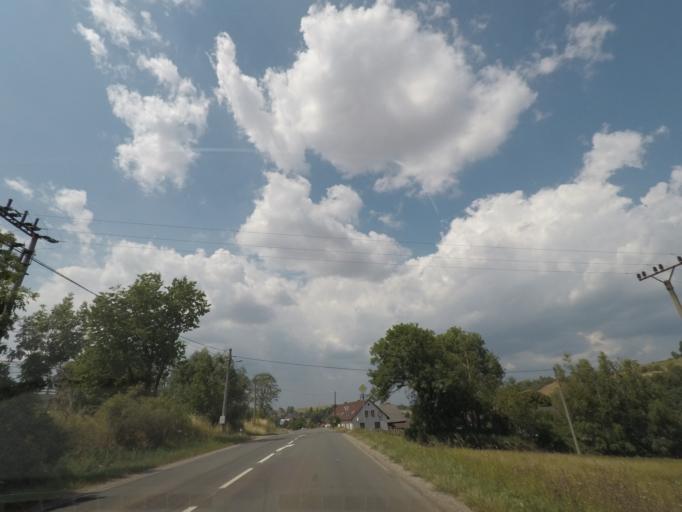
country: CZ
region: Kralovehradecky
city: Zadni Mostek
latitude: 50.5399
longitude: 15.6493
